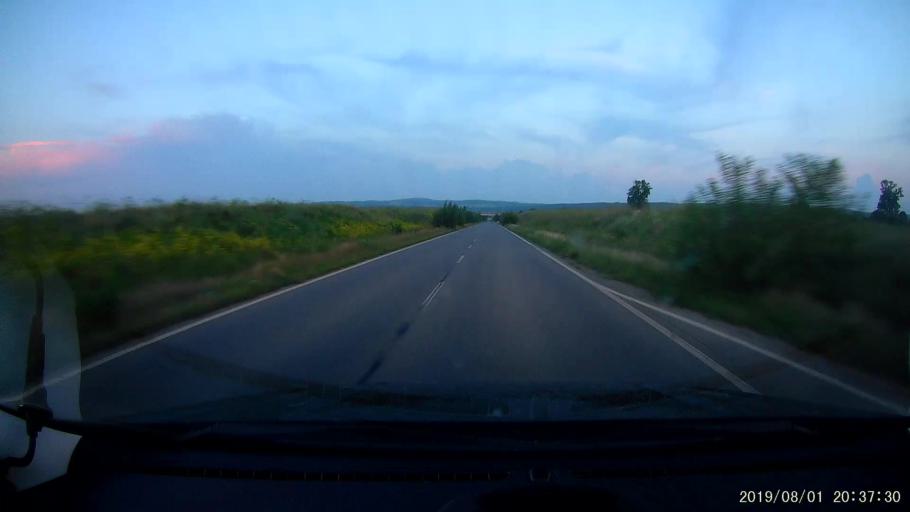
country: BG
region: Yambol
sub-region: Obshtina Elkhovo
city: Elkhovo
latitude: 42.0467
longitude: 26.5944
